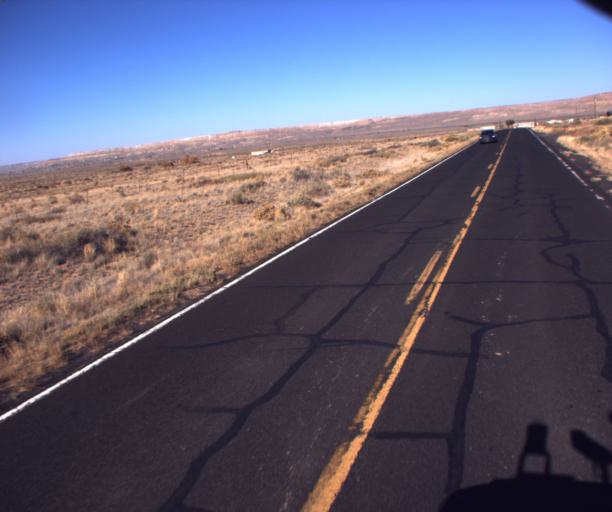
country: US
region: Arizona
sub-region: Navajo County
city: First Mesa
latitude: 35.8365
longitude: -110.3010
